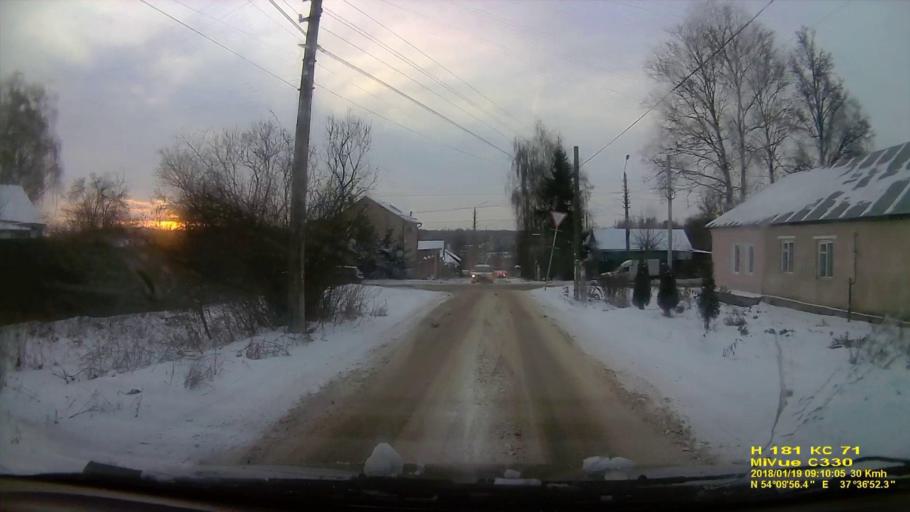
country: RU
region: Tula
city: Tula
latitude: 54.1656
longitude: 37.6146
